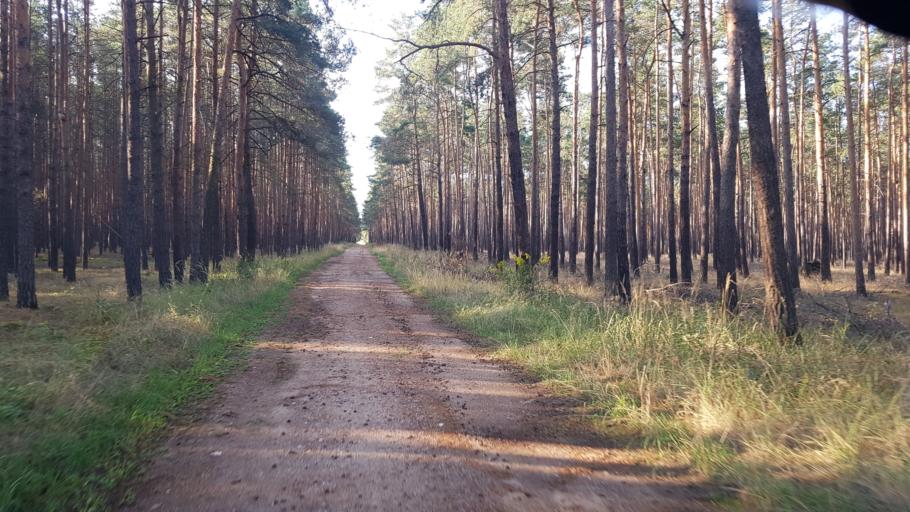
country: DE
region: Brandenburg
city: Sonnewalde
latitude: 51.6563
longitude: 13.6463
